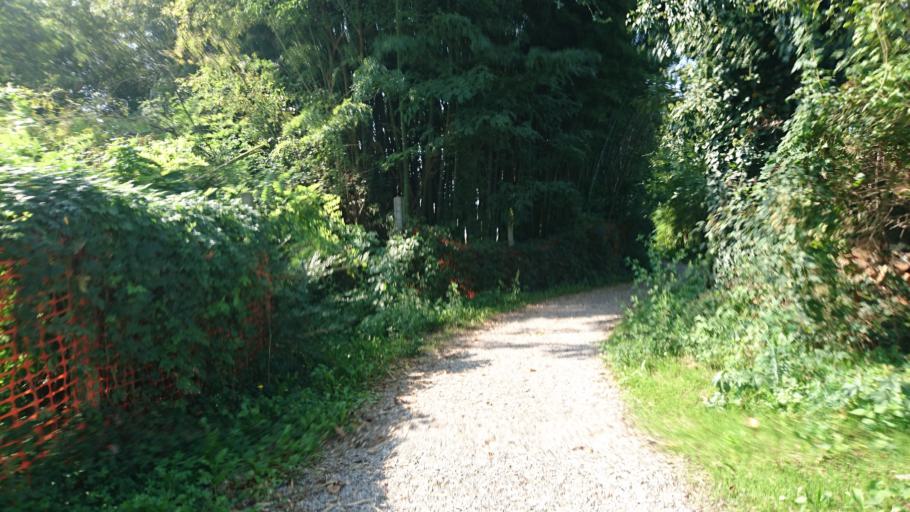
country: IT
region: Veneto
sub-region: Provincia di Padova
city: Piazzola sul Brenta
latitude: 45.5432
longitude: 11.8026
